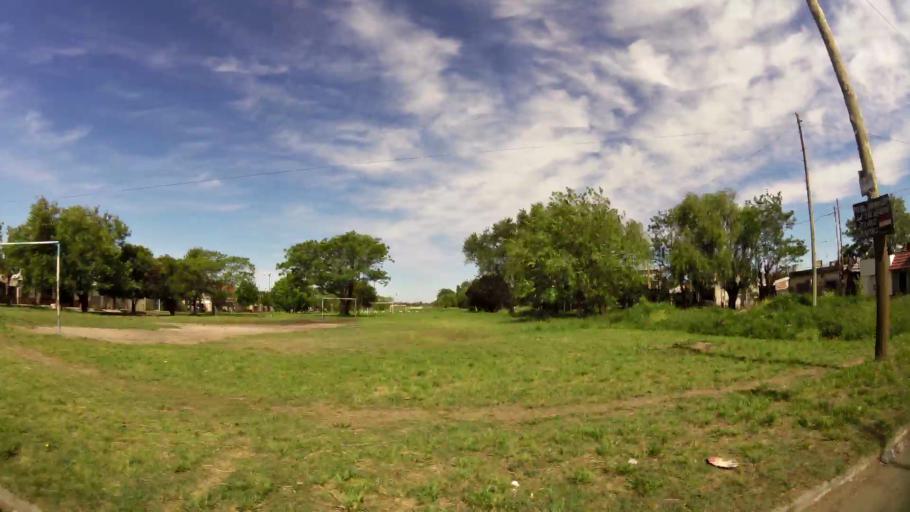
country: AR
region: Buenos Aires
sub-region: Partido de Almirante Brown
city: Adrogue
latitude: -34.7850
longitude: -58.3109
